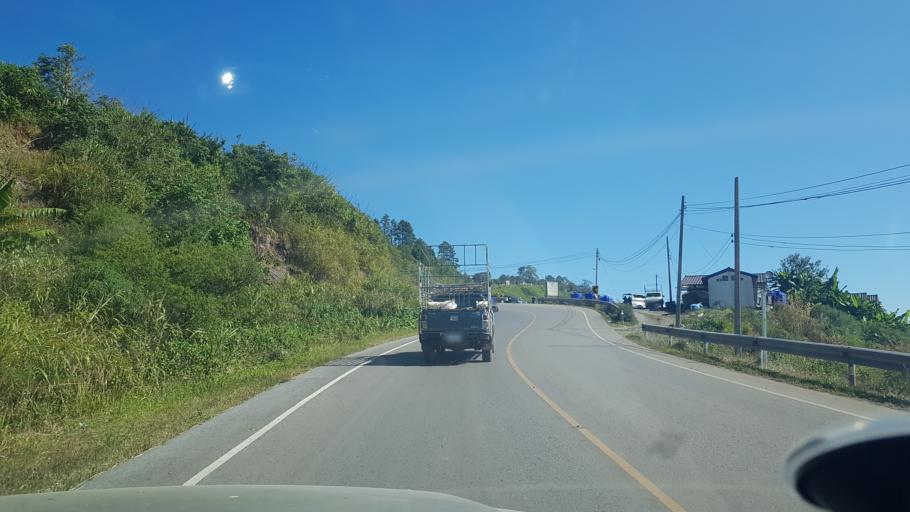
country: TH
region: Phetchabun
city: Lom Kao
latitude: 16.8900
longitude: 101.0963
